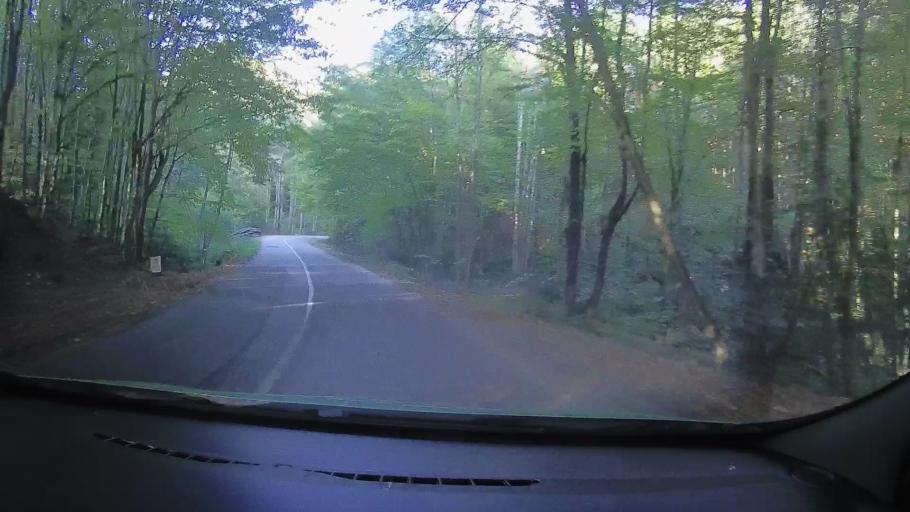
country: RO
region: Timis
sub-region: Comuna Nadrag
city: Nadrag
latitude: 45.6701
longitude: 22.1661
